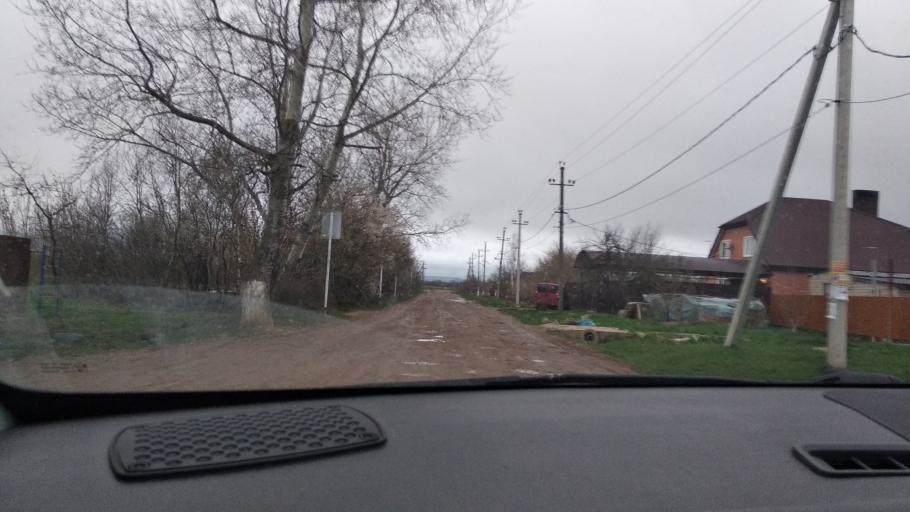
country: RU
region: Krasnodarskiy
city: Afipskiy
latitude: 44.8923
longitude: 38.7595
